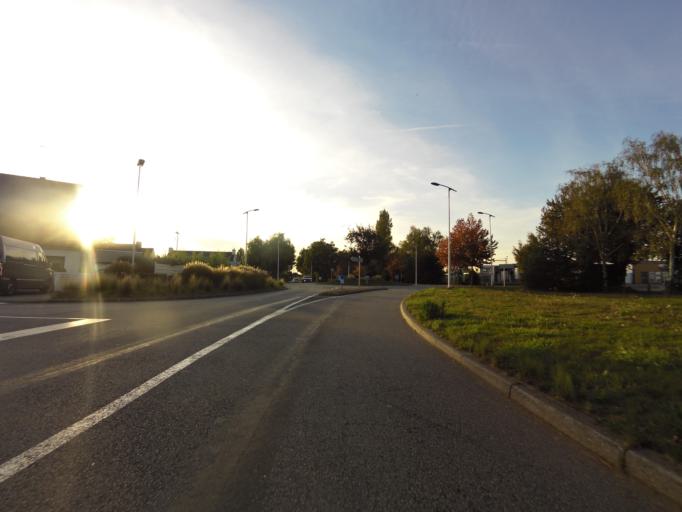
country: FR
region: Brittany
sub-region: Departement du Morbihan
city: Theix
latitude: 47.6317
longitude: -2.6616
